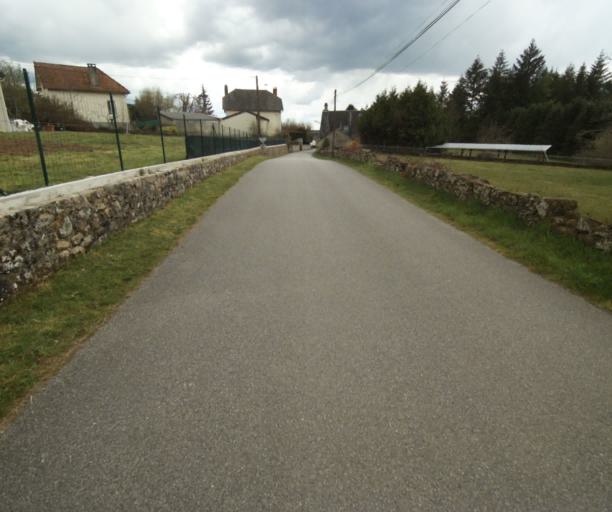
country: FR
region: Limousin
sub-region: Departement de la Correze
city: Correze
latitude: 45.2828
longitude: 1.9705
